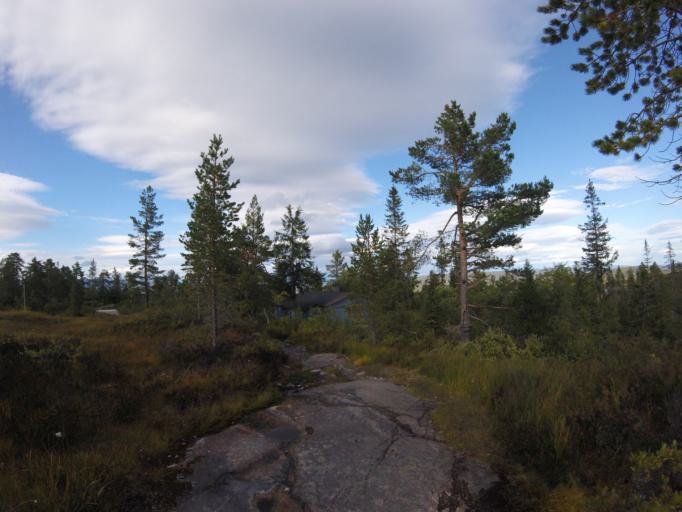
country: NO
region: Buskerud
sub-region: Flesberg
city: Lampeland
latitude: 59.7855
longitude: 9.4154
